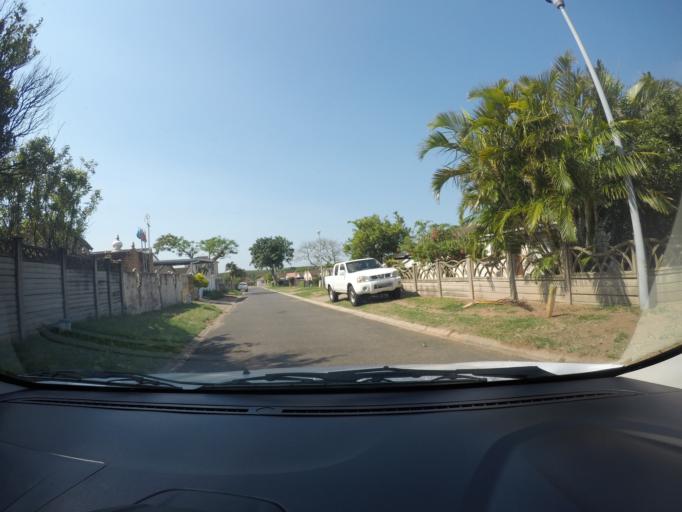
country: ZA
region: KwaZulu-Natal
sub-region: uThungulu District Municipality
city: Richards Bay
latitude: -28.7219
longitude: 32.0440
